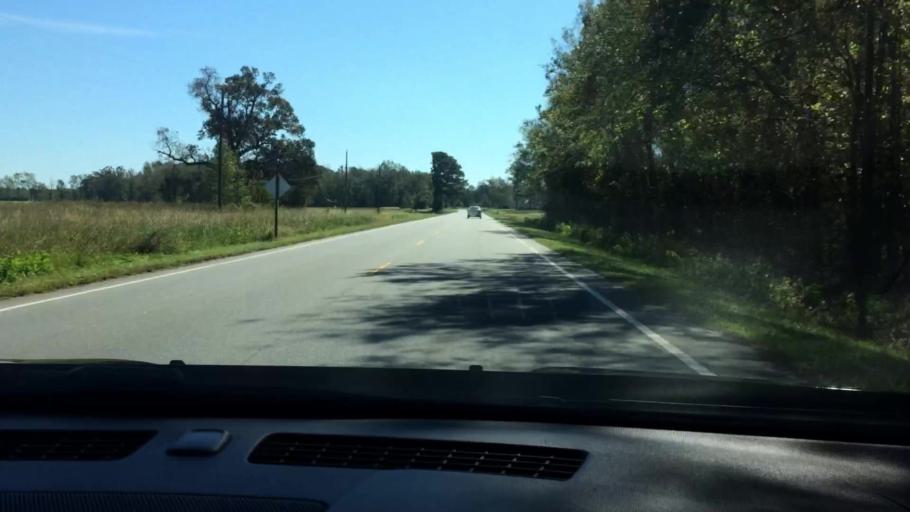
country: US
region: North Carolina
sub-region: Pitt County
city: Grifton
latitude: 35.3593
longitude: -77.3436
